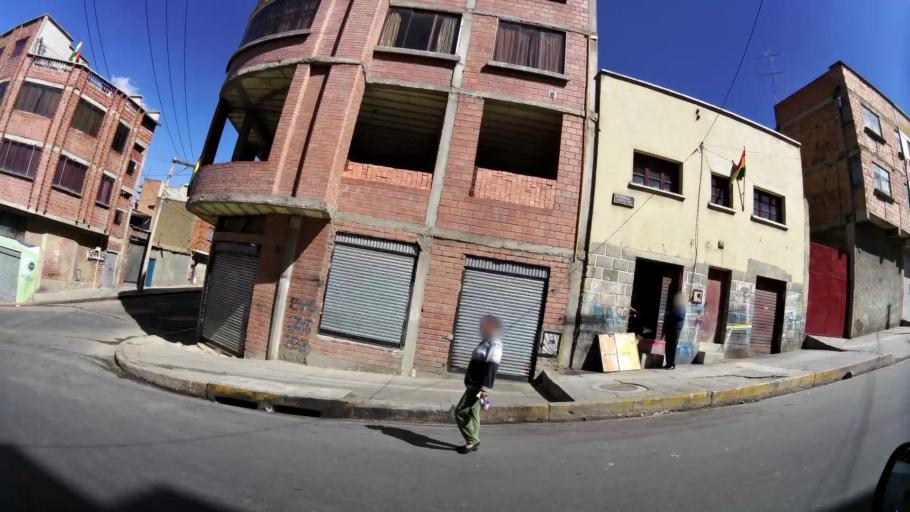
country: BO
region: La Paz
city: La Paz
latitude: -16.4937
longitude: -68.1563
